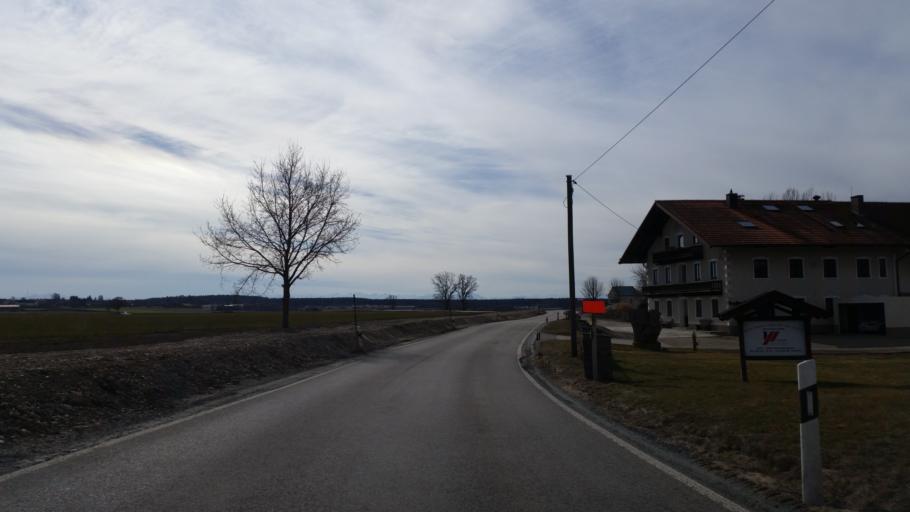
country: DE
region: Bavaria
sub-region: Upper Bavaria
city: Oberpframmern
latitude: 48.0373
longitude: 11.8131
